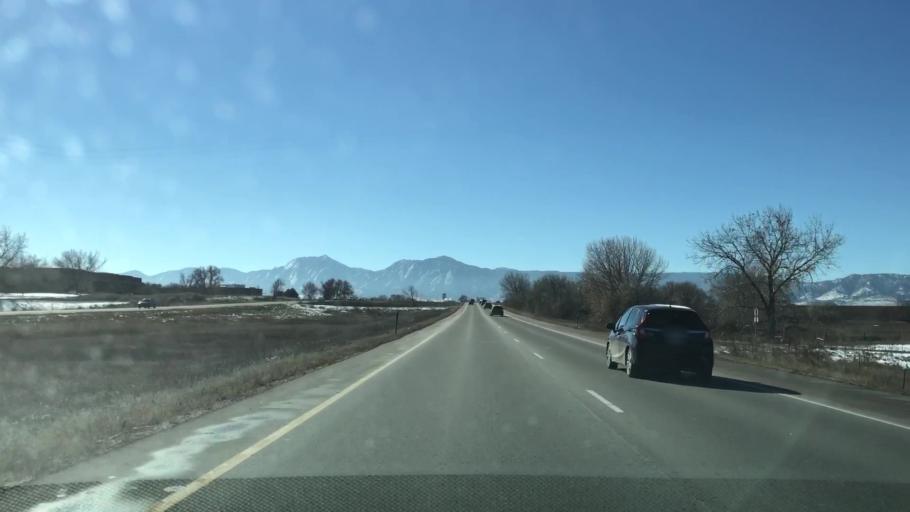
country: US
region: Colorado
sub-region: Boulder County
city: Gunbarrel
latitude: 40.0702
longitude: -105.2124
